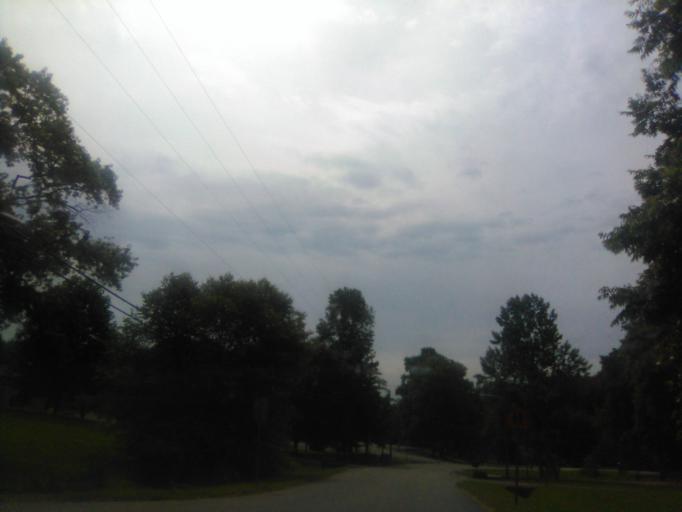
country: US
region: Tennessee
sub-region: Davidson County
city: Belle Meade
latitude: 36.0925
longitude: -86.8951
